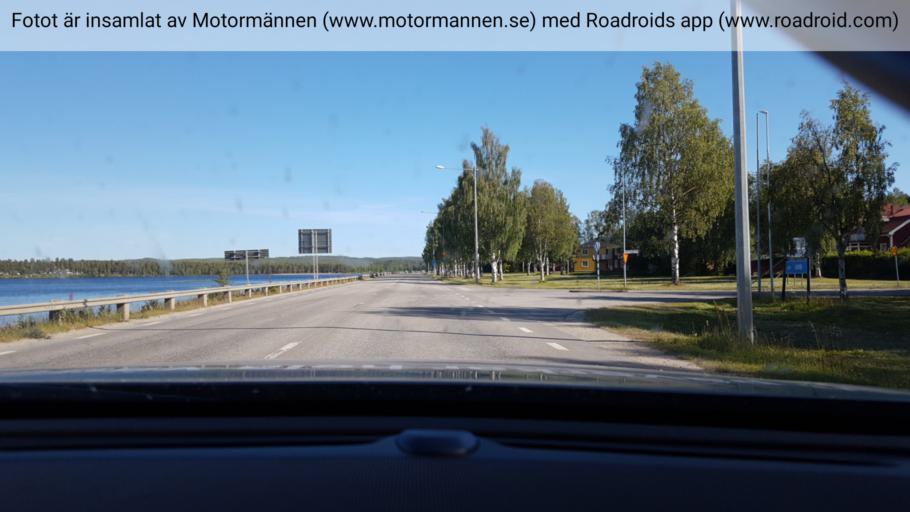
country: SE
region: Vaesterbotten
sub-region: Lycksele Kommun
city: Lycksele
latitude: 64.6011
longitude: 18.6760
